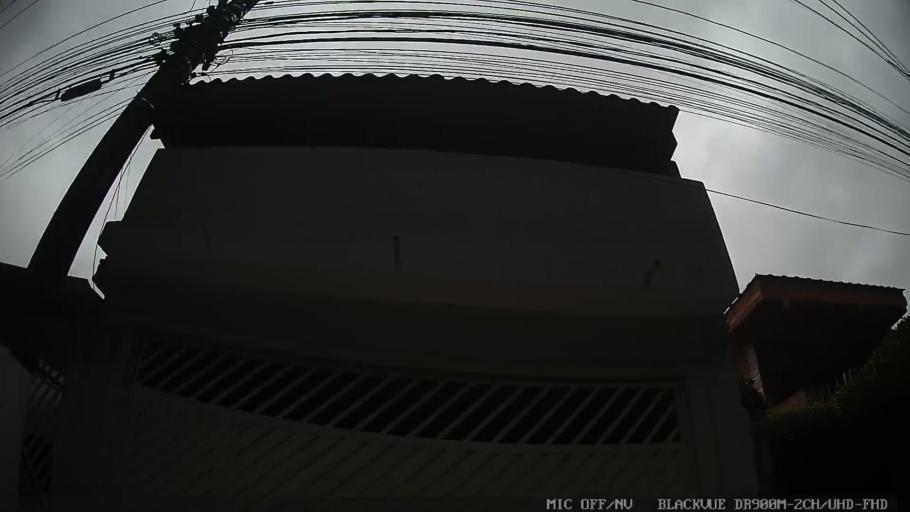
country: BR
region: Sao Paulo
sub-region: Osasco
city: Osasco
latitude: -23.4550
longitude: -46.7558
